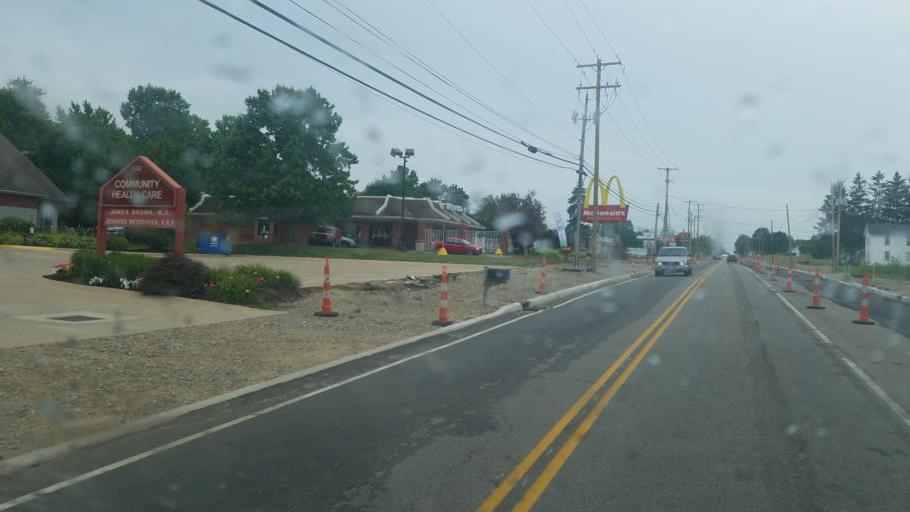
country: US
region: Ohio
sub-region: Summit County
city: Manchester
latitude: 40.9629
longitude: -81.5658
